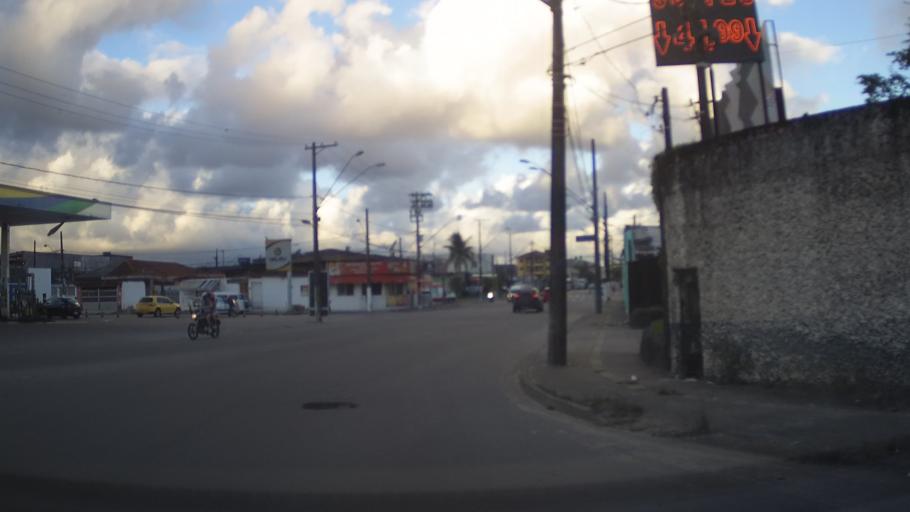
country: BR
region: Sao Paulo
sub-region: Sao Vicente
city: Sao Vicente
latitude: -23.9509
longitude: -46.4077
